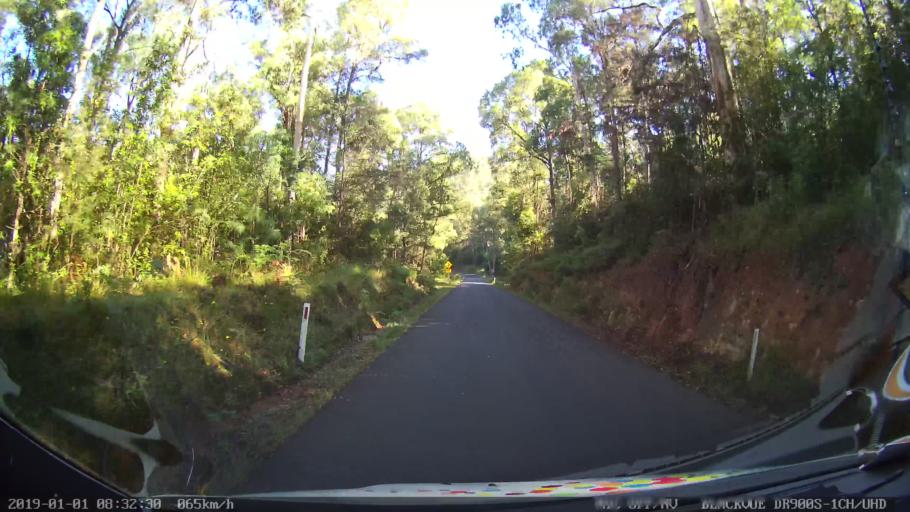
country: AU
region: New South Wales
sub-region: Snowy River
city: Jindabyne
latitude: -36.3614
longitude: 148.2061
